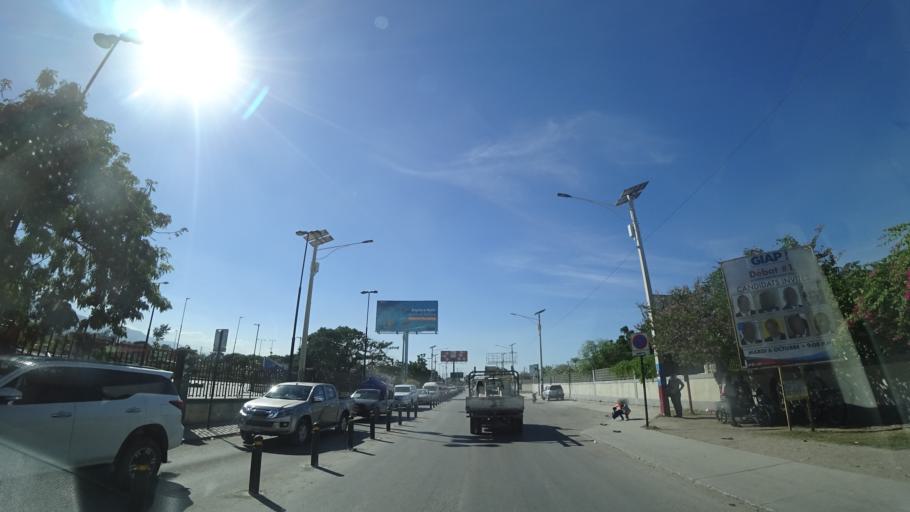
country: HT
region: Ouest
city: Delmas 73
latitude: 18.5752
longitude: -72.2978
